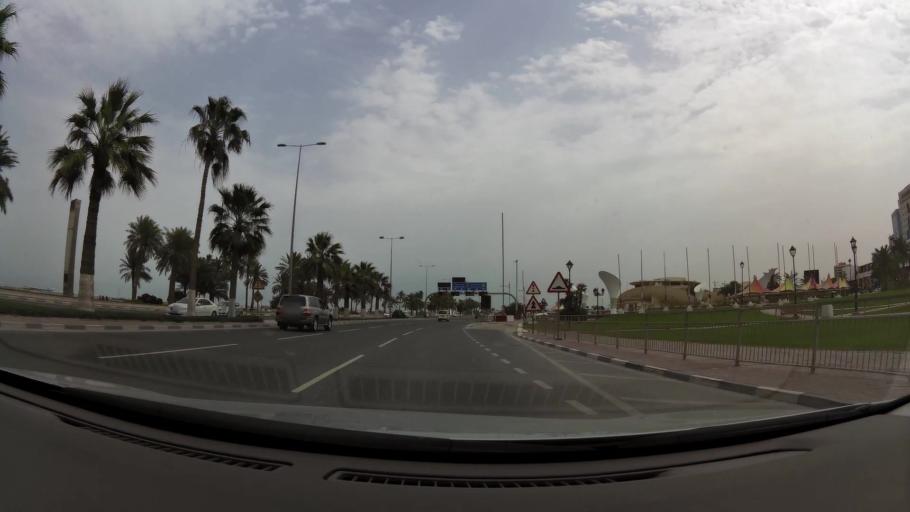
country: QA
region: Baladiyat ad Dawhah
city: Doha
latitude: 25.2909
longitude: 51.5481
